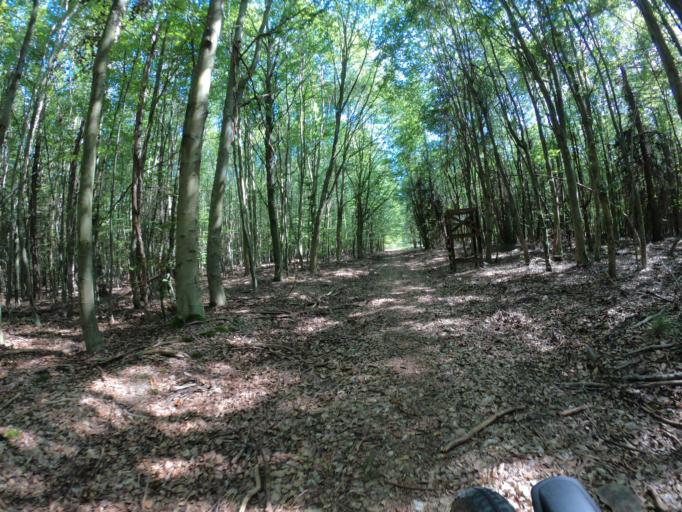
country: DE
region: Hesse
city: Morfelden-Walldorf
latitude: 50.0051
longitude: 8.6257
